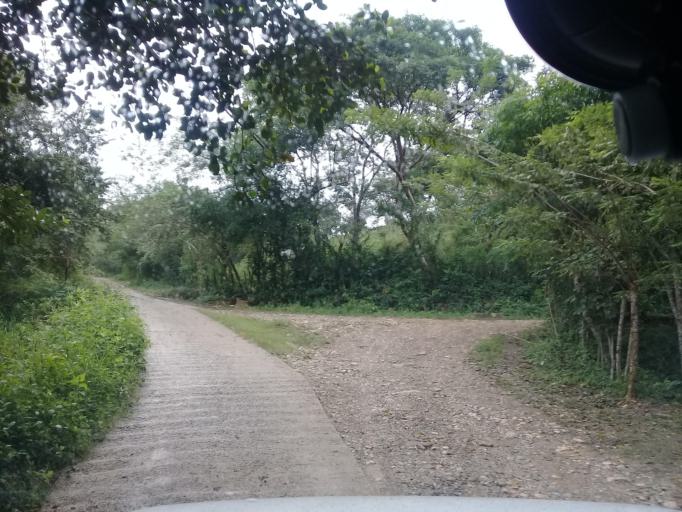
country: MX
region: Veracruz
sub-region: Chalma
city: San Pedro Coyutla
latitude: 21.2490
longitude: -98.4125
